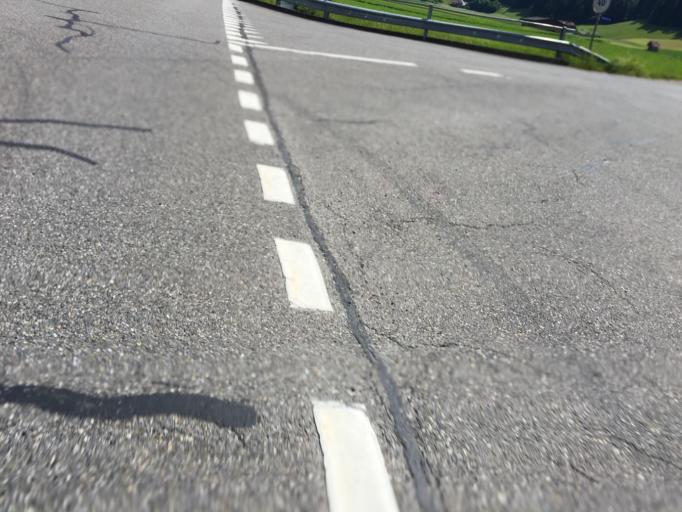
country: CH
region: Bern
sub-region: Bern-Mittelland District
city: Zaziwil
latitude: 46.8923
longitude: 7.6501
